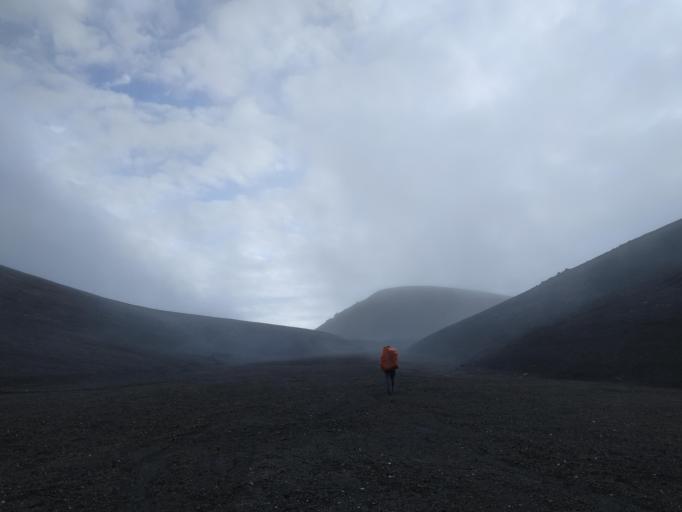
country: RU
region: Kamtsjatka
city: Petropavlovsk-Kamchatsky
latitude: 53.2797
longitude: 158.7650
